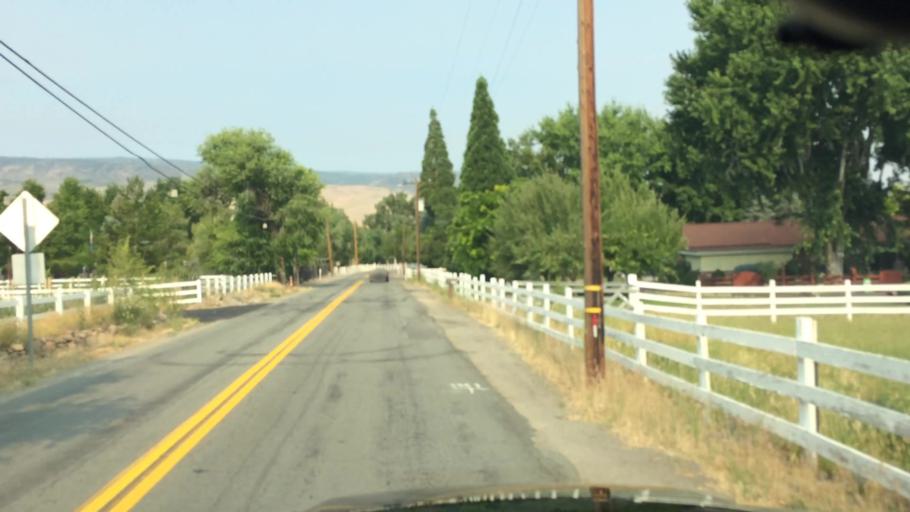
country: US
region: Nevada
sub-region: Washoe County
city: Reno
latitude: 39.4404
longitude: -119.7910
